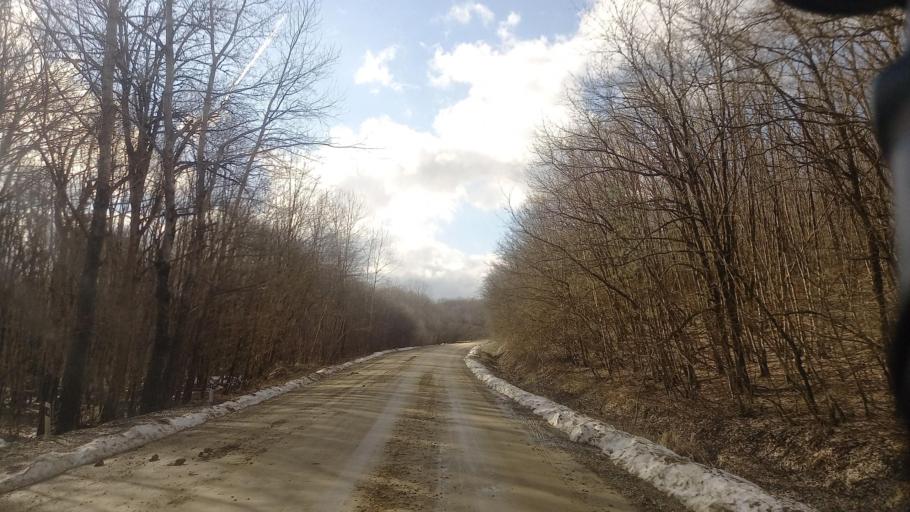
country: RU
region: Krasnodarskiy
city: Smolenskaya
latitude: 44.5959
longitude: 38.8287
